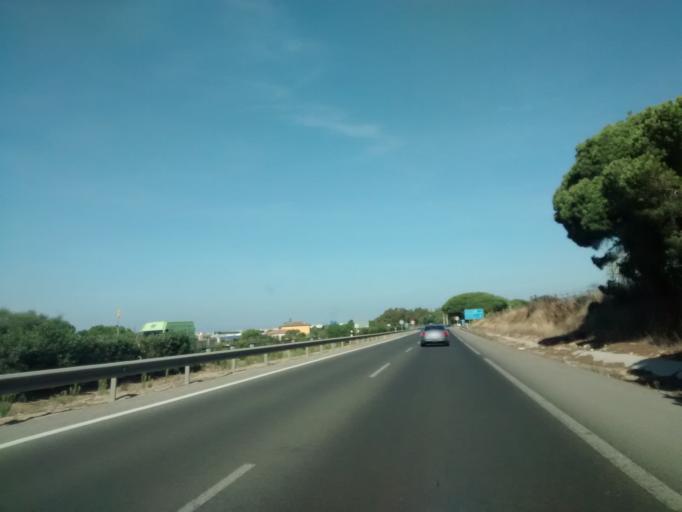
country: ES
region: Andalusia
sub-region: Provincia de Cadiz
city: Chiclana de la Frontera
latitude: 36.4428
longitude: -6.1338
